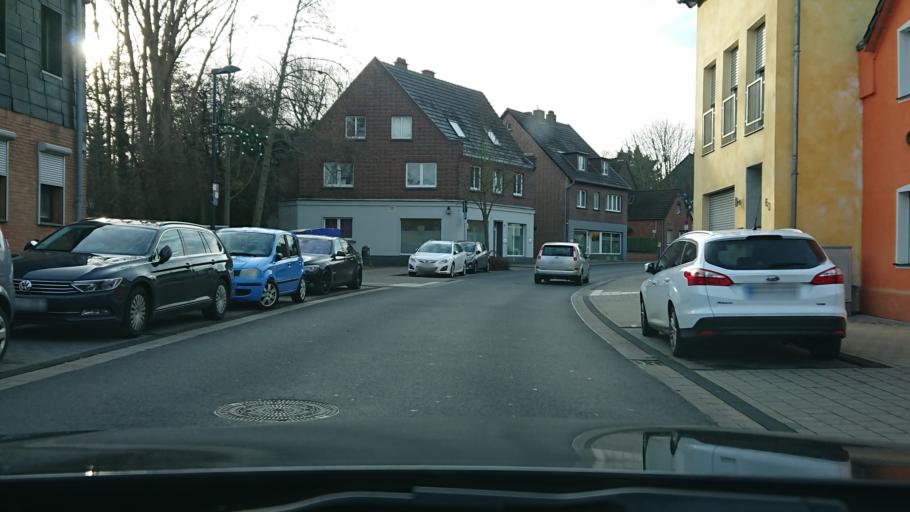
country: DE
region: North Rhine-Westphalia
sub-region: Regierungsbezirk Koln
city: Frechen
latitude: 50.8887
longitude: 6.8330
